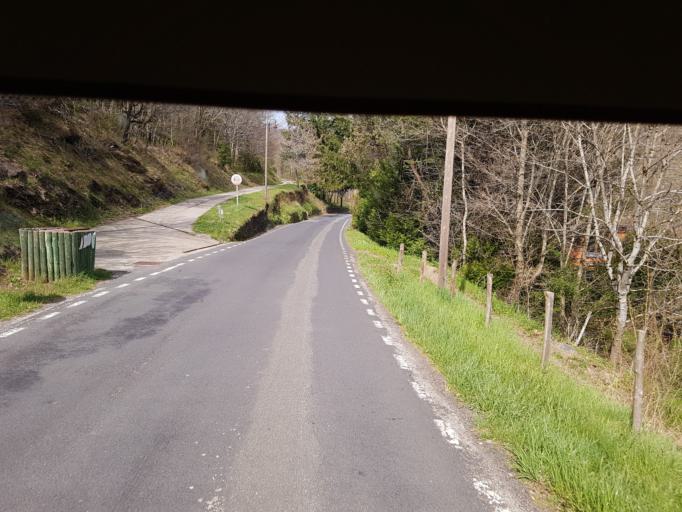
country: FR
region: Languedoc-Roussillon
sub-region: Departement de la Lozere
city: Florac
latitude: 44.2516
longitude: 3.5808
